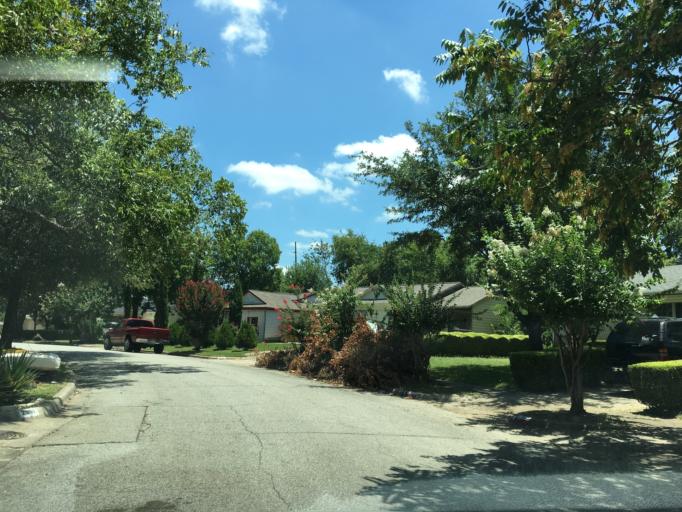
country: US
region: Texas
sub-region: Dallas County
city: Garland
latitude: 32.8492
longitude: -96.6671
